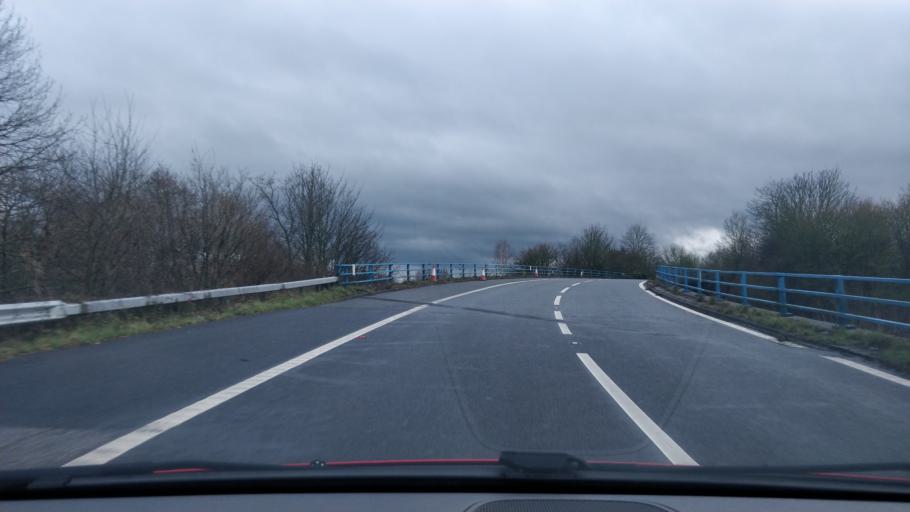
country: GB
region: England
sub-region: Knowsley
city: Knowsley
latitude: 53.4357
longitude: -2.8538
